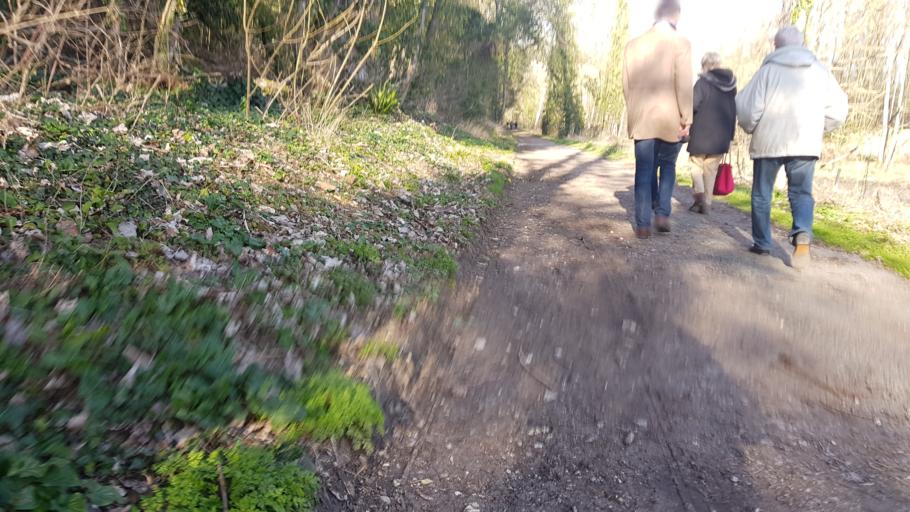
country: FR
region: Poitou-Charentes
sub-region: Departement de la Vienne
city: Migne-Auxances
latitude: 46.6278
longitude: 0.3211
